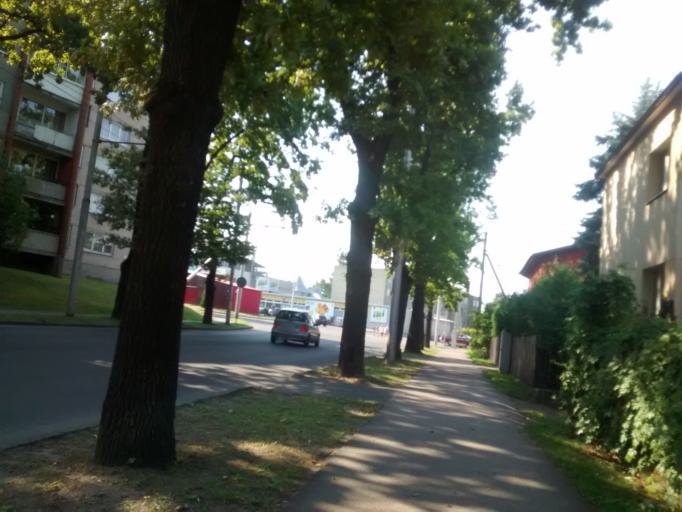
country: LT
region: Kauno apskritis
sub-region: Kaunas
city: Eiguliai
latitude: 54.9152
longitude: 23.9206
